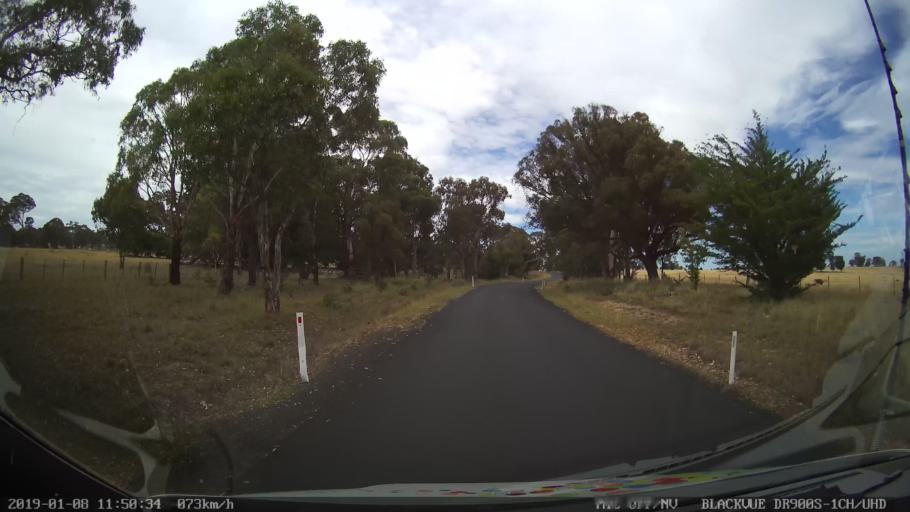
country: AU
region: New South Wales
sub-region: Armidale Dumaresq
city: Armidale
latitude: -30.3841
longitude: 151.5575
